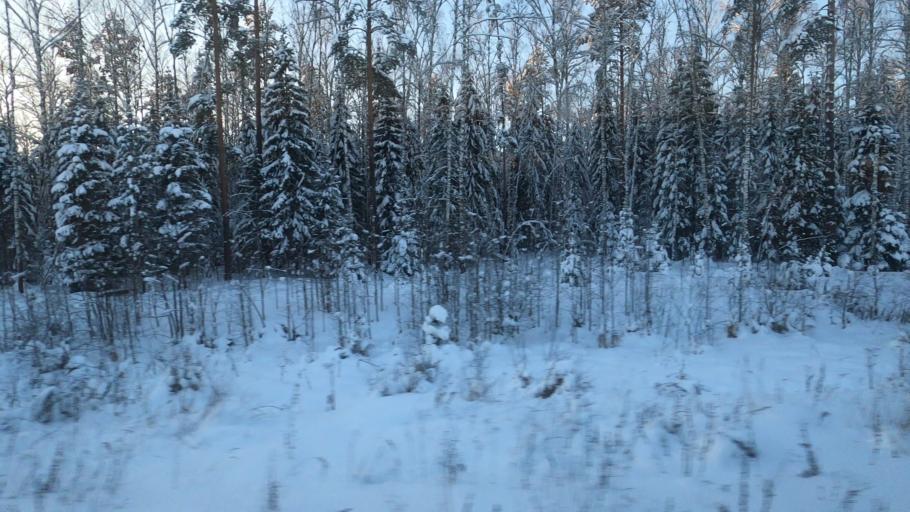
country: RU
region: Moskovskaya
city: Zhukovka
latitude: 56.5032
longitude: 37.5533
